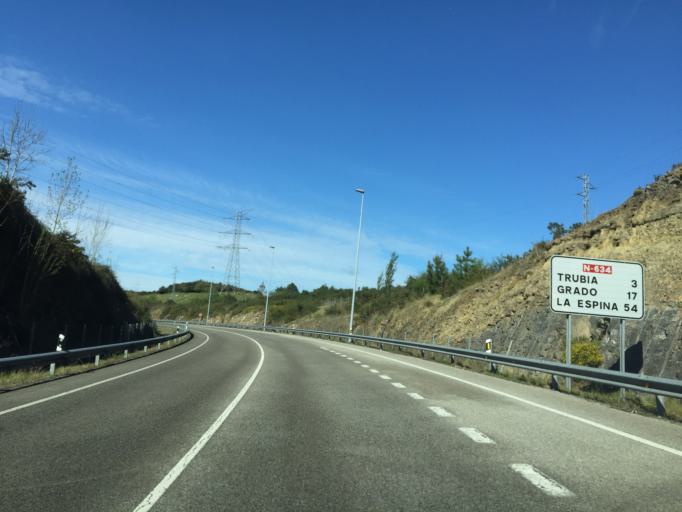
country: ES
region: Asturias
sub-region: Province of Asturias
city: Llanera
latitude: 43.3660
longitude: -5.9560
